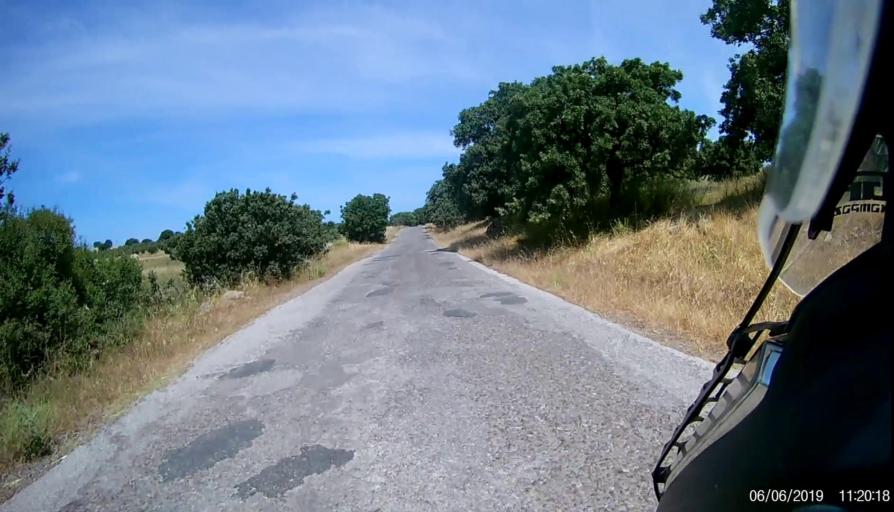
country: TR
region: Canakkale
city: Gulpinar
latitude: 39.6650
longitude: 26.1637
